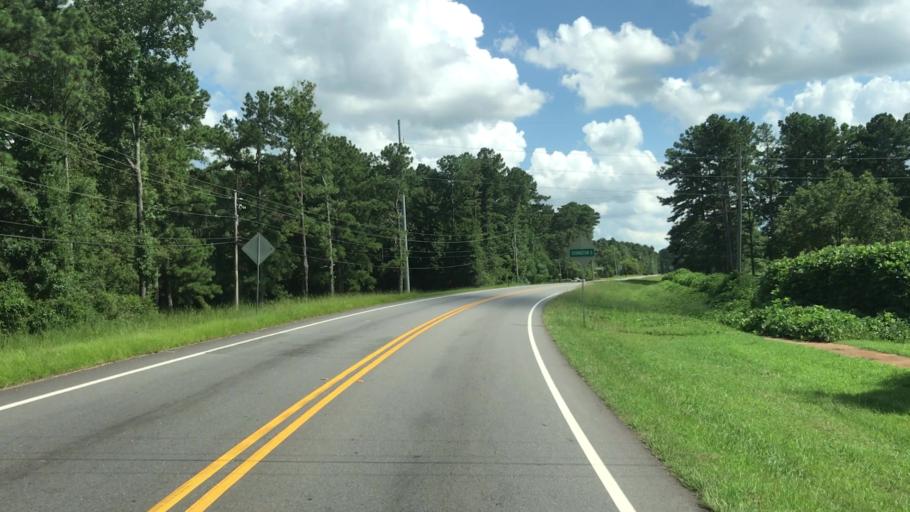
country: US
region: Georgia
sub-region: Newton County
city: Oxford
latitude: 33.6671
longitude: -83.8511
